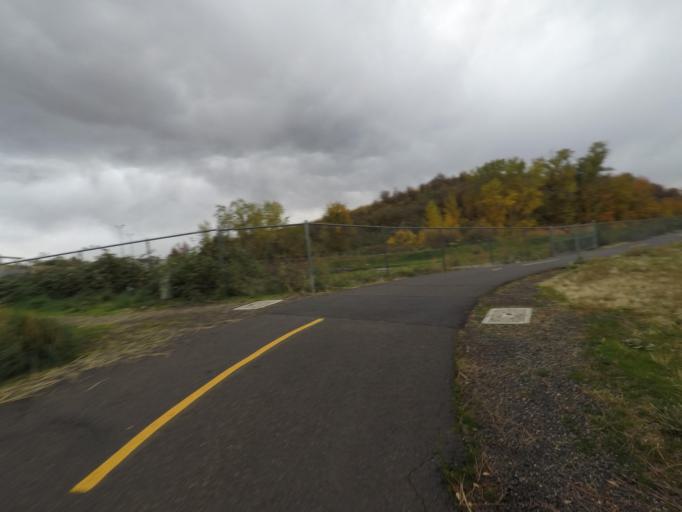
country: US
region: Washington
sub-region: Walla Walla County
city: Walla Walla East
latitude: 46.0804
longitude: -118.2545
